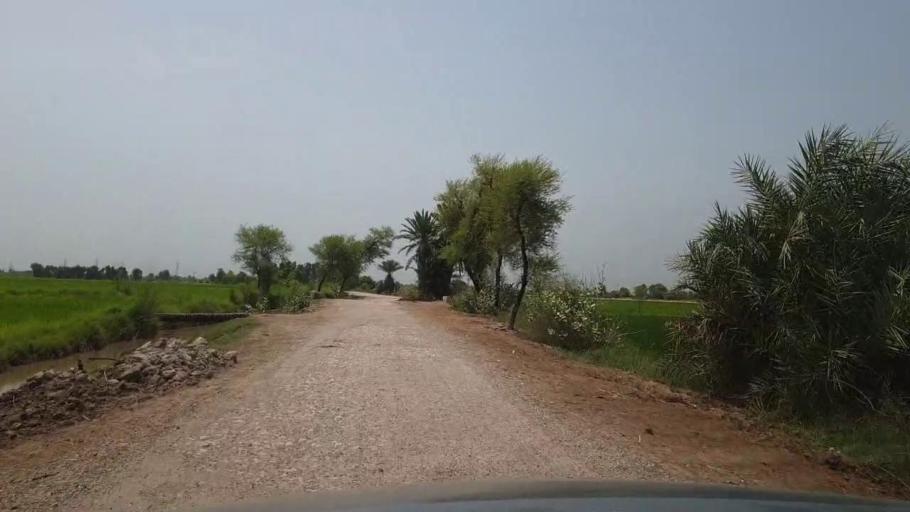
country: PK
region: Sindh
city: Madeji
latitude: 27.7764
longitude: 68.4322
